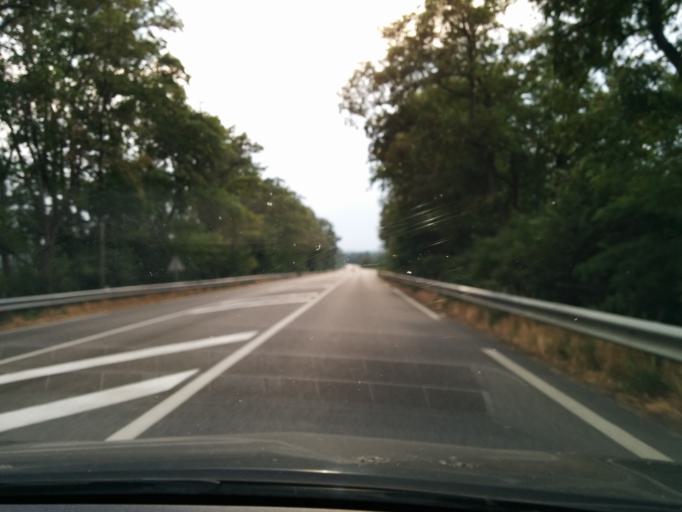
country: FR
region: Midi-Pyrenees
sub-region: Departement de la Haute-Garonne
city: Baziege
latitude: 43.4491
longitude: 1.6294
